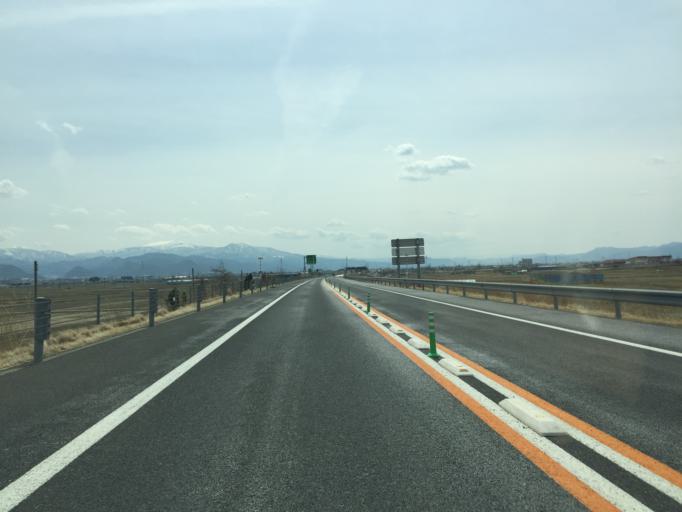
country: JP
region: Yamagata
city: Tendo
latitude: 38.3766
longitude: 140.3470
